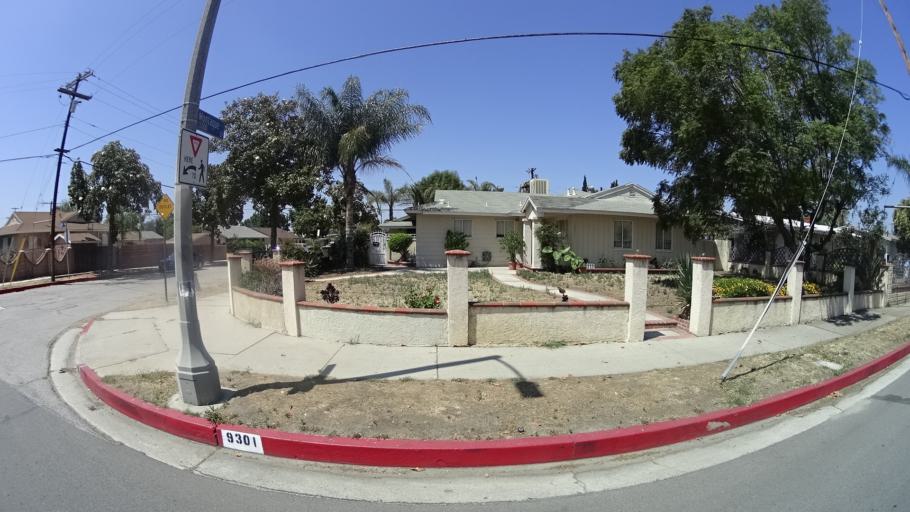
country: US
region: California
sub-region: Los Angeles County
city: San Fernando
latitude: 34.2392
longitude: -118.4231
